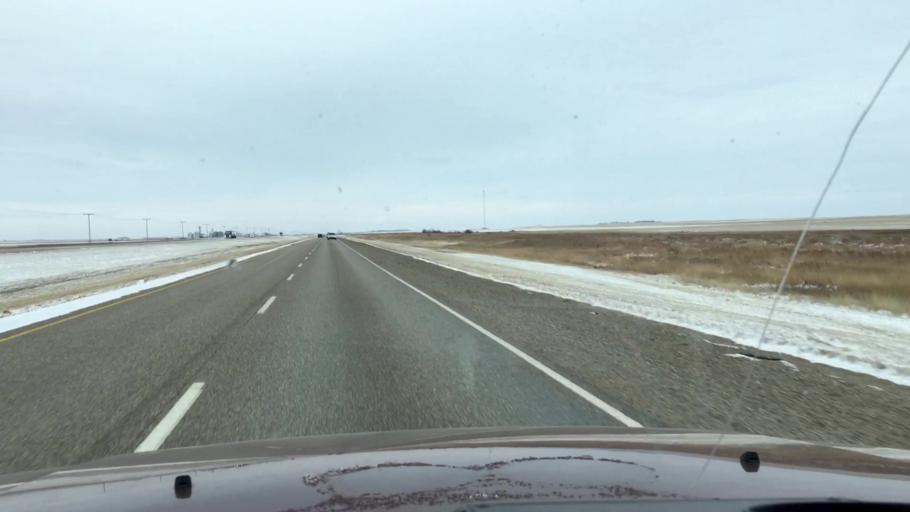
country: CA
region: Saskatchewan
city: Moose Jaw
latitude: 51.0239
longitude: -105.7904
